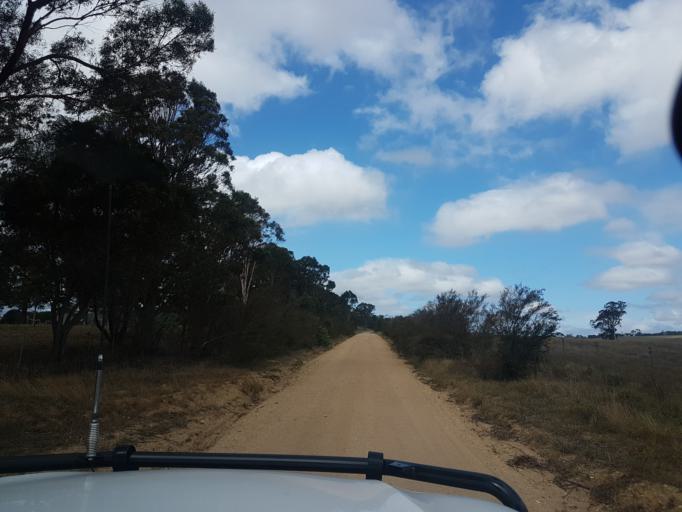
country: AU
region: Victoria
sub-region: East Gippsland
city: Bairnsdale
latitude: -37.7859
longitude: 147.5570
